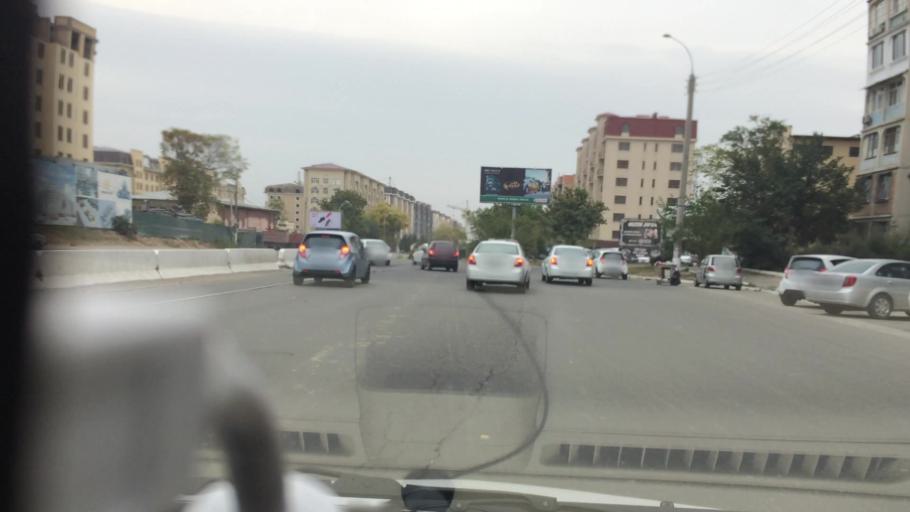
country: UZ
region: Toshkent
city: Salor
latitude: 41.3124
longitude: 69.3317
